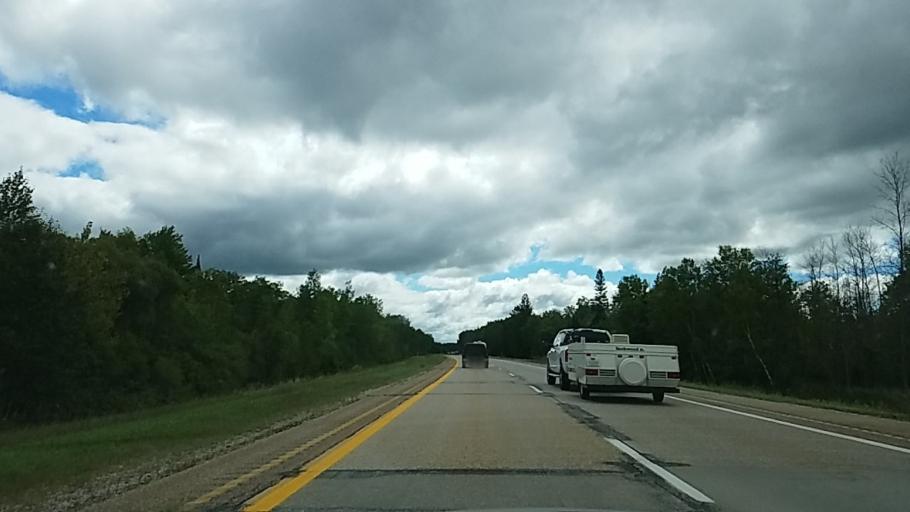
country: US
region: Michigan
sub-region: Ogemaw County
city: West Branch
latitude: 44.2159
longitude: -84.2046
